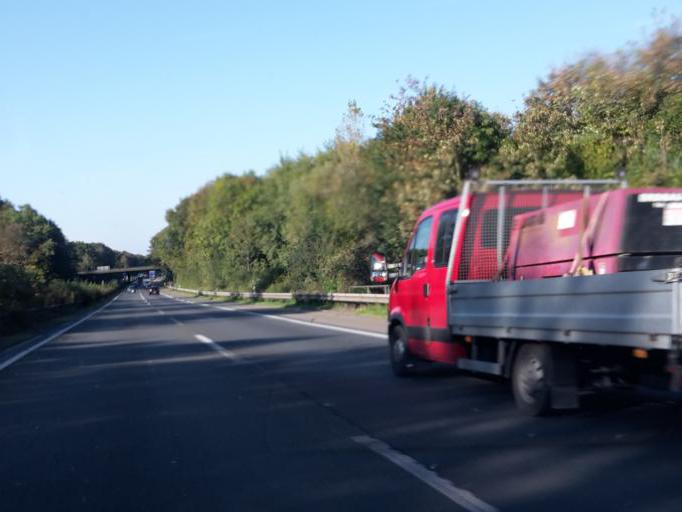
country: DE
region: North Rhine-Westphalia
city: Kamen
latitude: 51.6234
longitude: 7.6884
